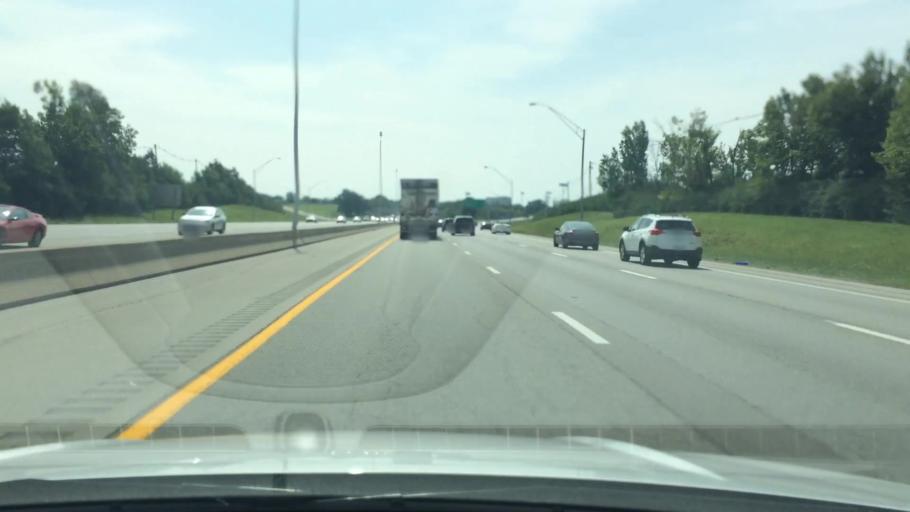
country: US
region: Kentucky
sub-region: Fayette County
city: Lexington-Fayette
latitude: 38.0277
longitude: -84.4169
